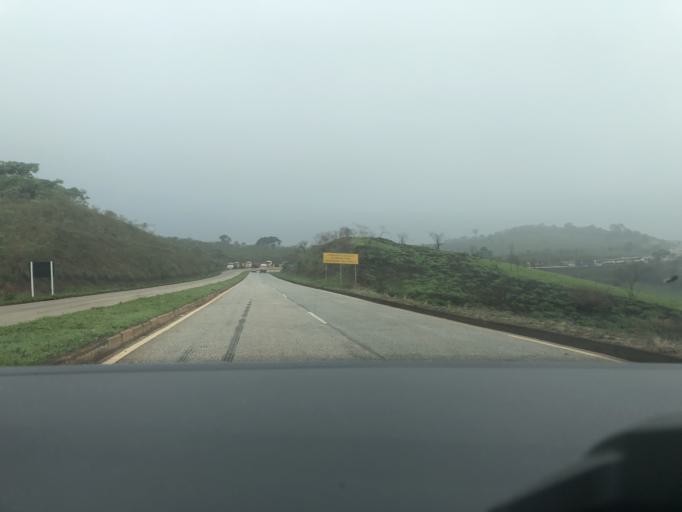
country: BR
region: Minas Gerais
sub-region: Congonhas
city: Congonhas
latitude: -20.5936
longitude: -43.9556
